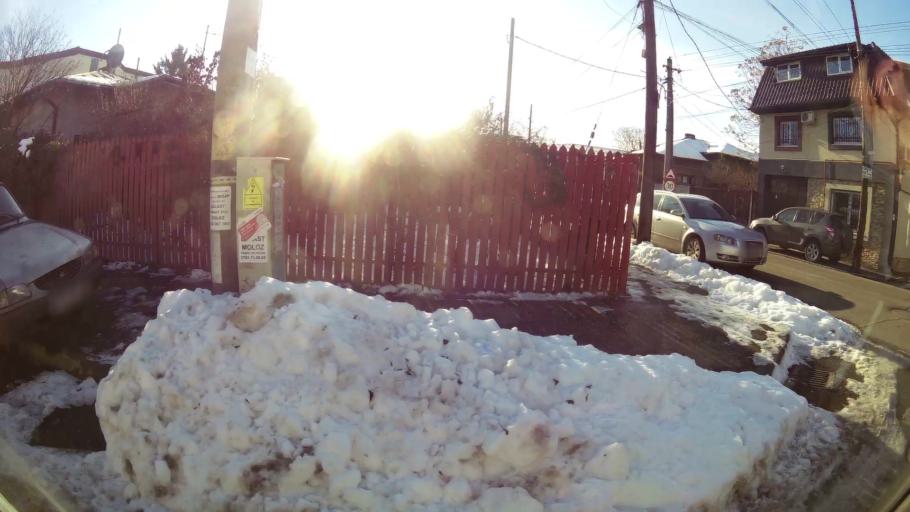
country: RO
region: Bucuresti
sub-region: Municipiul Bucuresti
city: Bucuresti
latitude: 44.4040
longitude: 26.0894
